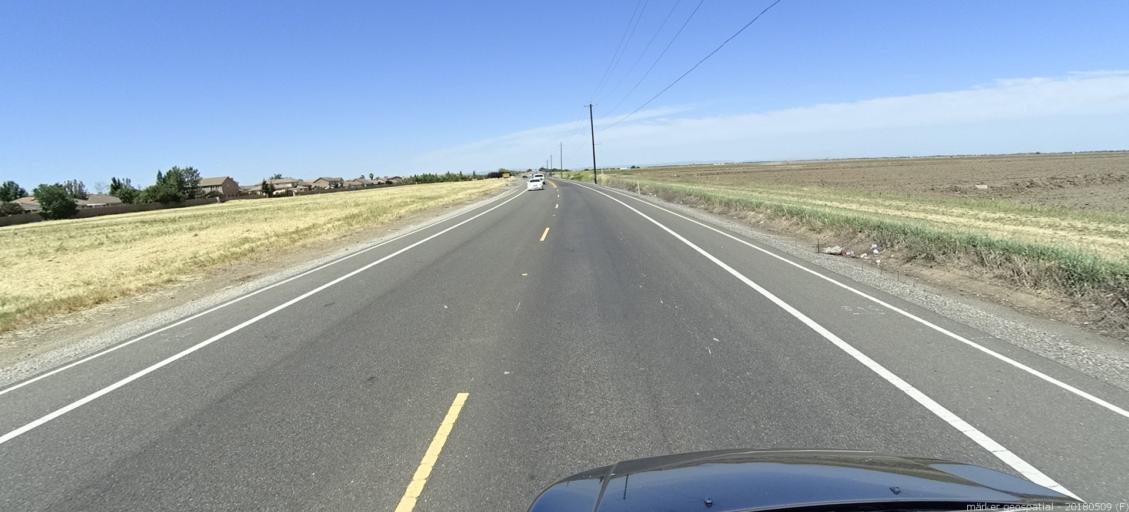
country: US
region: California
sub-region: Sacramento County
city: Elverta
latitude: 38.6856
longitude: -121.5259
